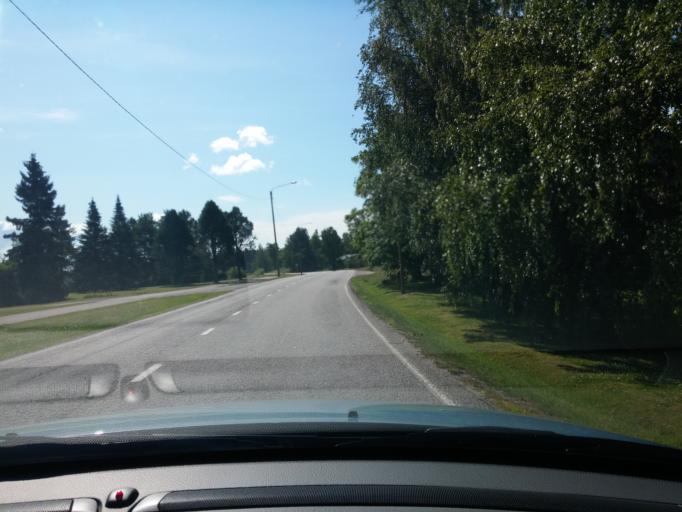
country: FI
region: Uusimaa
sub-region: Porvoo
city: Askola
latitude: 60.4922
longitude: 25.5415
